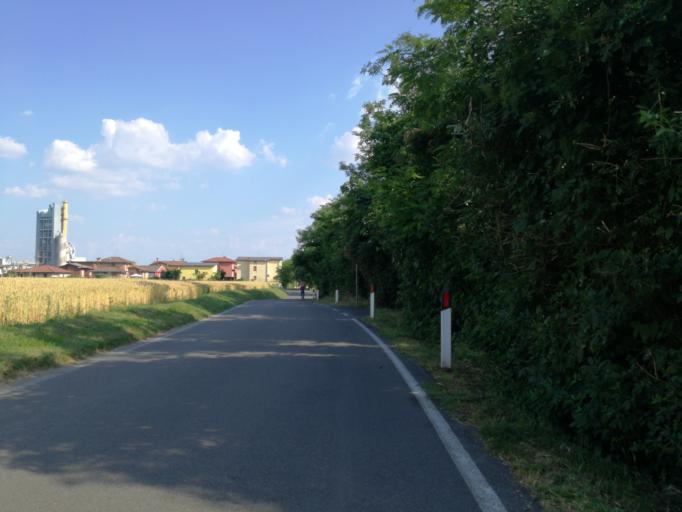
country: IT
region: Lombardy
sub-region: Provincia di Bergamo
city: Calusco d'Adda
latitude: 45.6881
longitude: 9.4574
